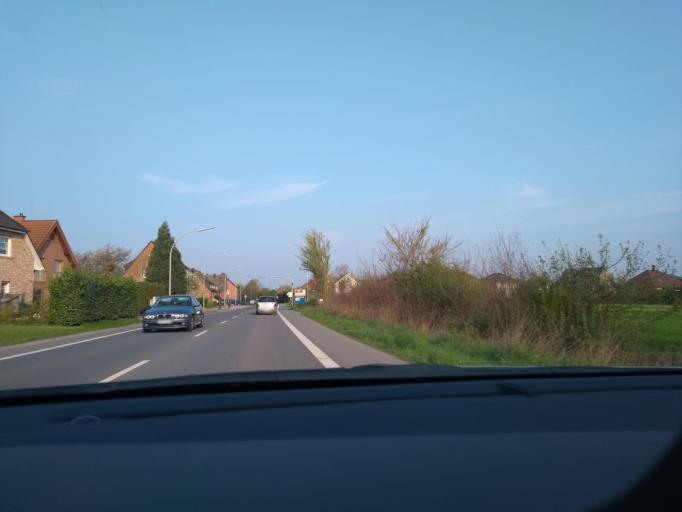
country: DE
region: North Rhine-Westphalia
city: Selm
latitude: 51.6952
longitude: 7.4798
